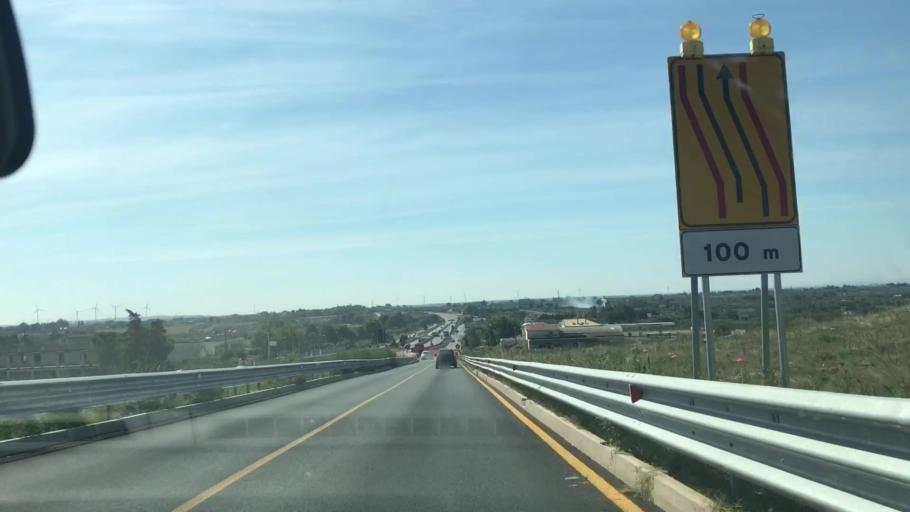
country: IT
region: Apulia
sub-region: Provincia di Bari
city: Altamura
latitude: 40.8082
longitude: 16.5556
